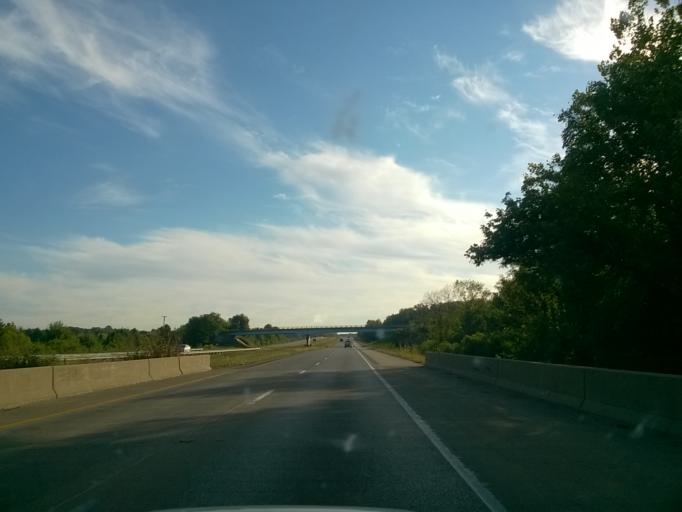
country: US
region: Indiana
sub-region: Warrick County
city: Chandler
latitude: 38.1872
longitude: -87.3556
